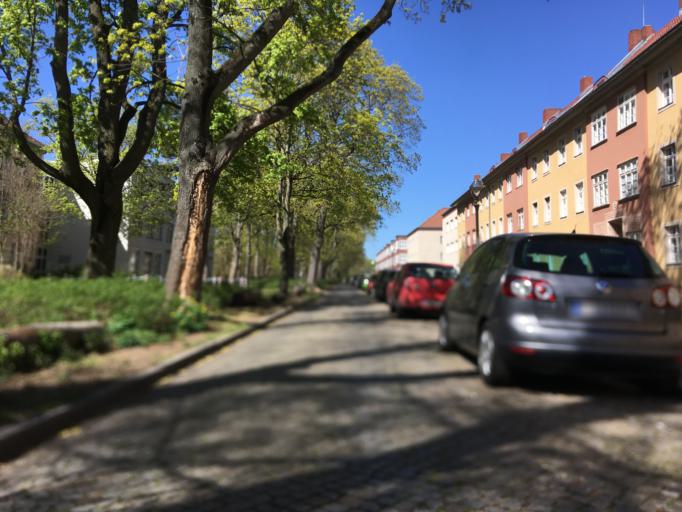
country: DE
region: Berlin
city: Tegel
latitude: 52.5923
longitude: 13.2974
